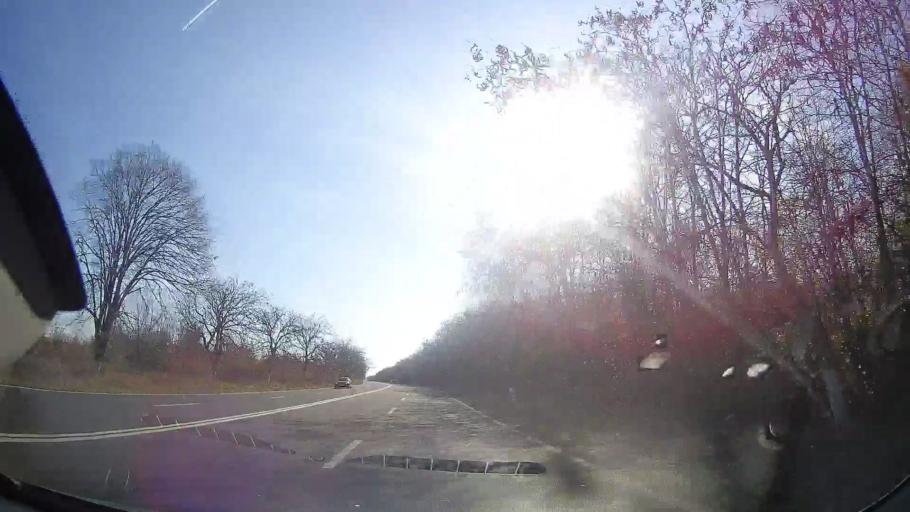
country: RO
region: Constanta
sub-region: Comuna Douazeci si Trei August
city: Dulcesti
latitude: 43.8849
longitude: 28.5732
